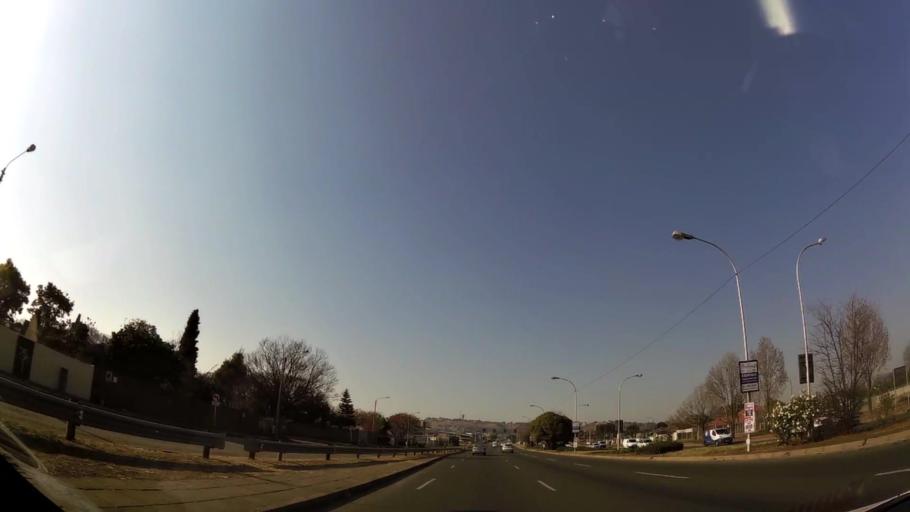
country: ZA
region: Gauteng
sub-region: City of Johannesburg Metropolitan Municipality
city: Modderfontein
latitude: -26.1542
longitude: 28.1616
